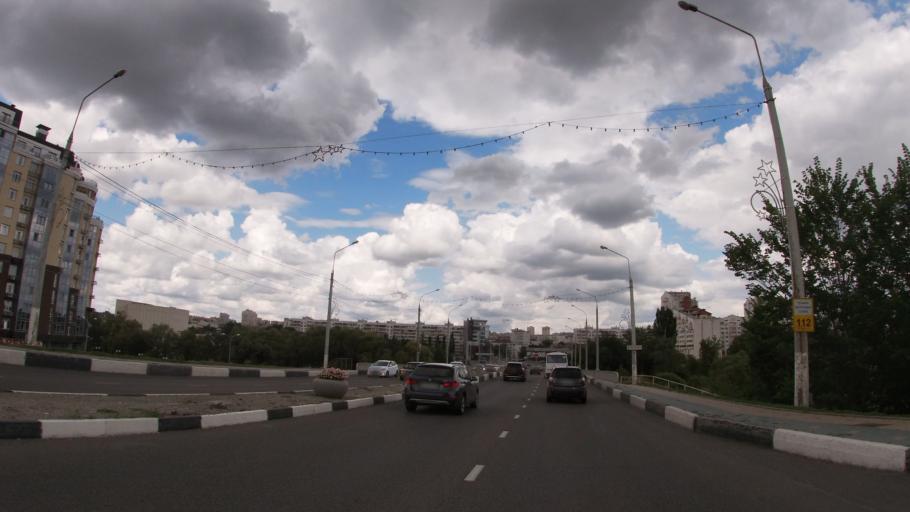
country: RU
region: Belgorod
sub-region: Belgorodskiy Rayon
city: Belgorod
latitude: 50.5889
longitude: 36.5893
